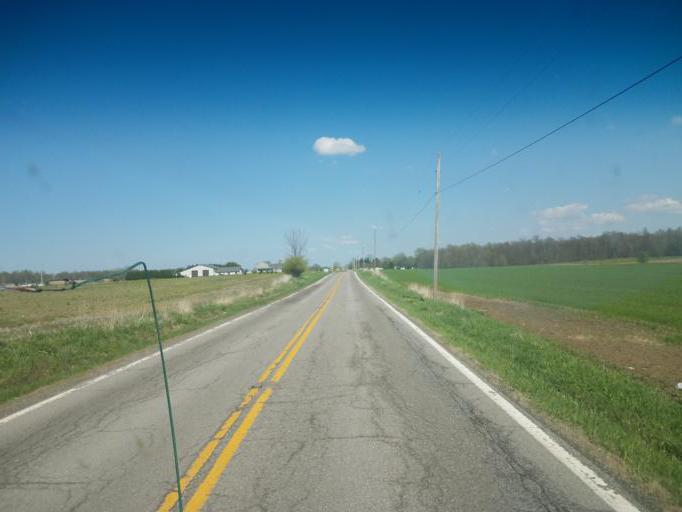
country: US
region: Ohio
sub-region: Wayne County
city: West Salem
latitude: 40.9212
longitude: -82.0895
